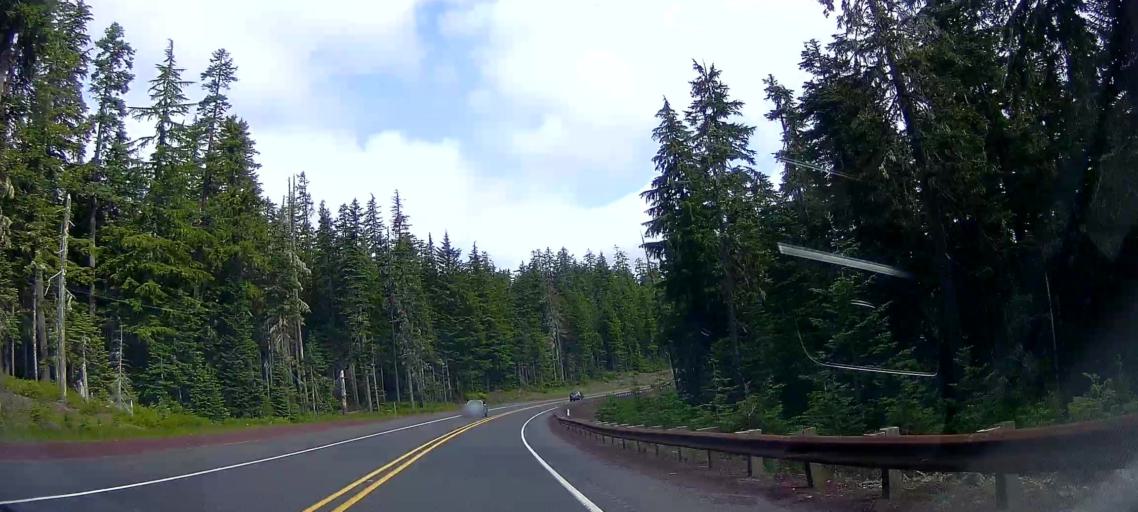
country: US
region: Oregon
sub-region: Clackamas County
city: Mount Hood Village
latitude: 45.2195
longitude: -121.6983
